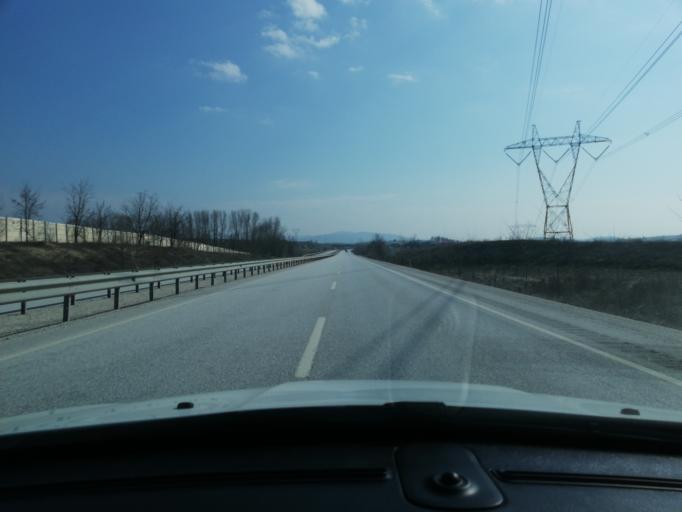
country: TR
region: Cankiri
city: Atkaracalar
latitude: 40.8380
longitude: 33.1570
